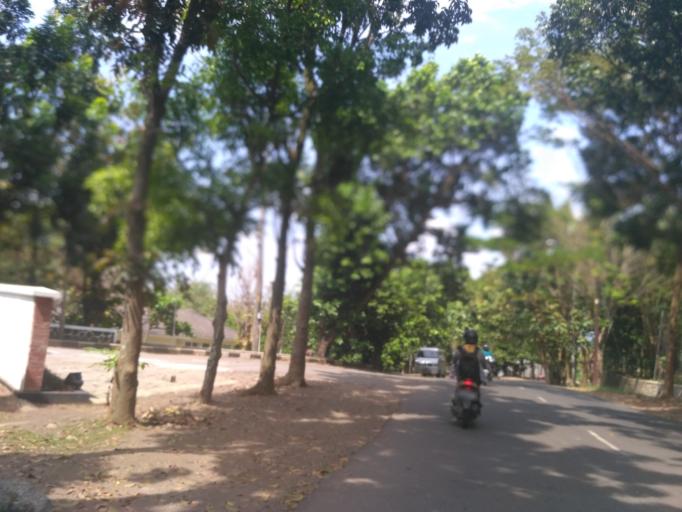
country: ID
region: Central Java
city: Semarang
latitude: -7.0530
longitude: 110.4414
